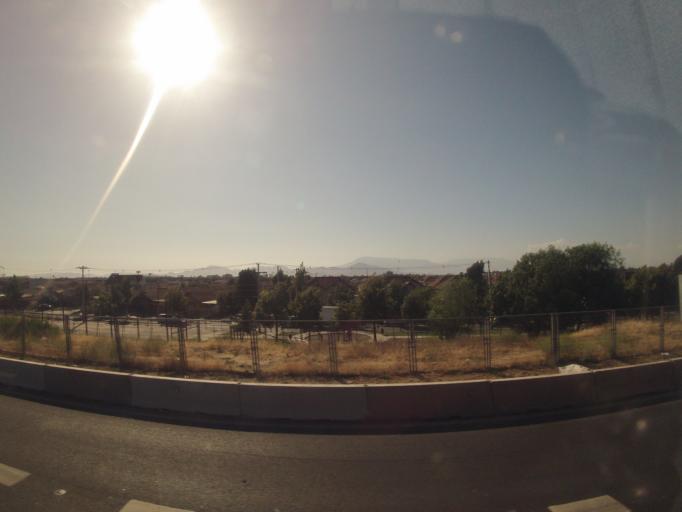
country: CL
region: Santiago Metropolitan
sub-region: Provincia de Santiago
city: Lo Prado
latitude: -33.5152
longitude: -70.7017
